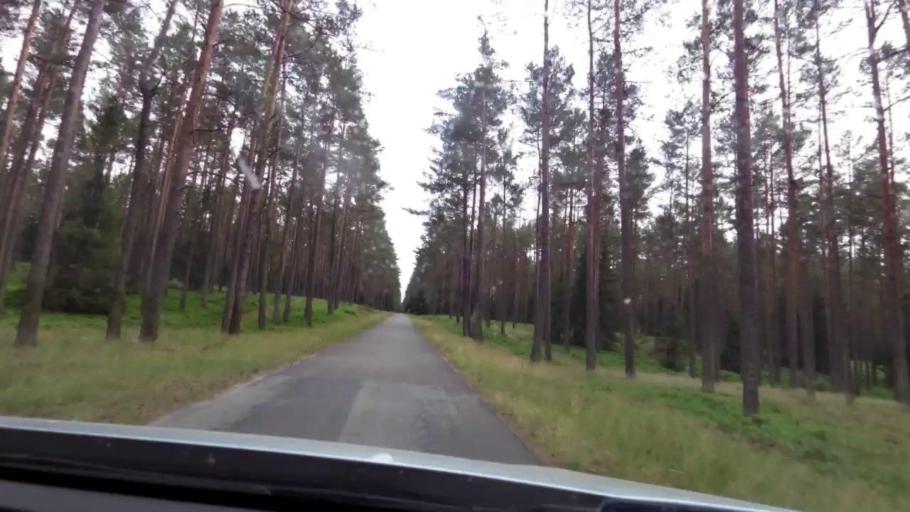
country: PL
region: Pomeranian Voivodeship
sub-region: Powiat bytowski
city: Trzebielino
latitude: 54.2181
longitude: 17.0033
